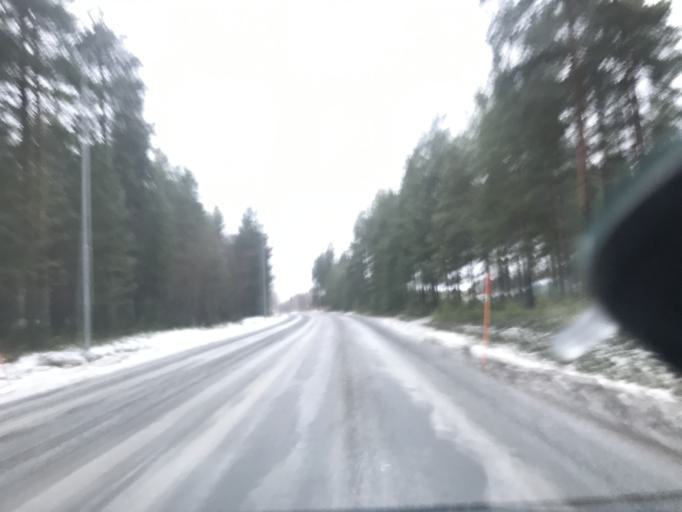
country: SE
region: Norrbotten
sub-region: Lulea Kommun
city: Sodra Sunderbyn
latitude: 65.6515
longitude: 21.9540
